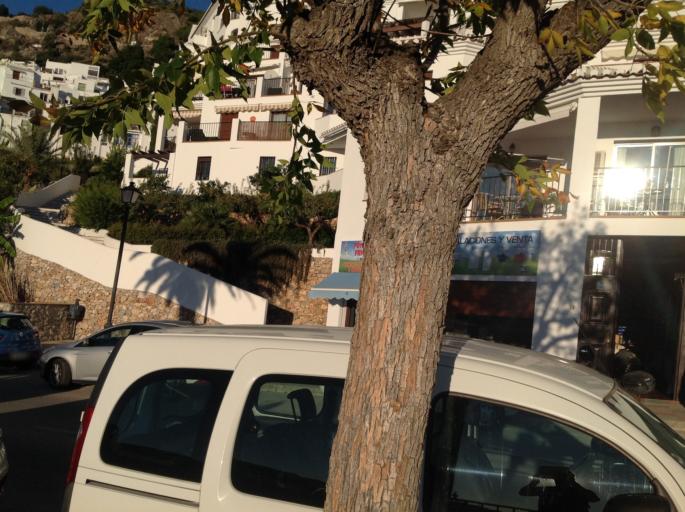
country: ES
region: Andalusia
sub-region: Provincia de Malaga
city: Frigiliana
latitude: 36.7910
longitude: -3.8976
